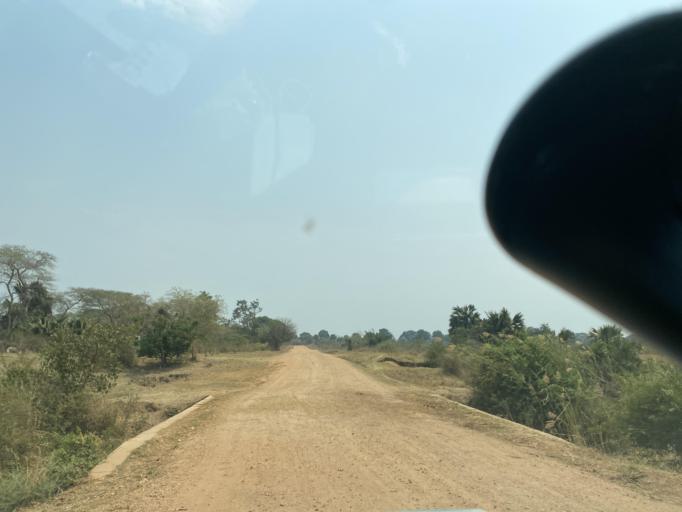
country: ZM
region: Lusaka
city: Kafue
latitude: -15.6293
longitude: 28.0989
